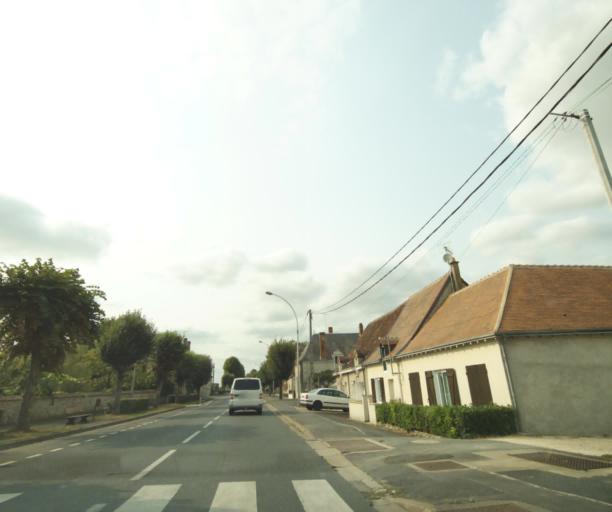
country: FR
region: Centre
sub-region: Departement de l'Indre
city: Chatillon-sur-Indre
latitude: 46.9931
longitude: 1.1647
